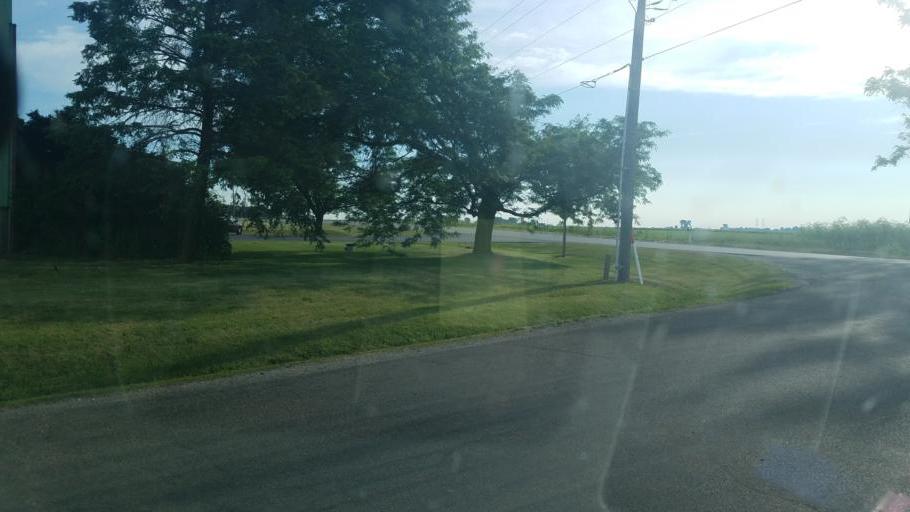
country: US
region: Illinois
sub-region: Peoria County
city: Hanna City
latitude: 40.7770
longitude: -89.7527
